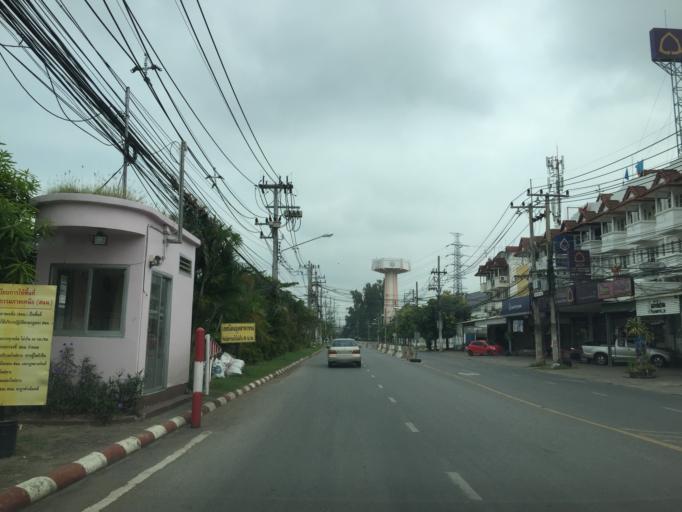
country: TH
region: Lamphun
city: Lamphun
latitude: 18.5869
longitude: 99.0507
